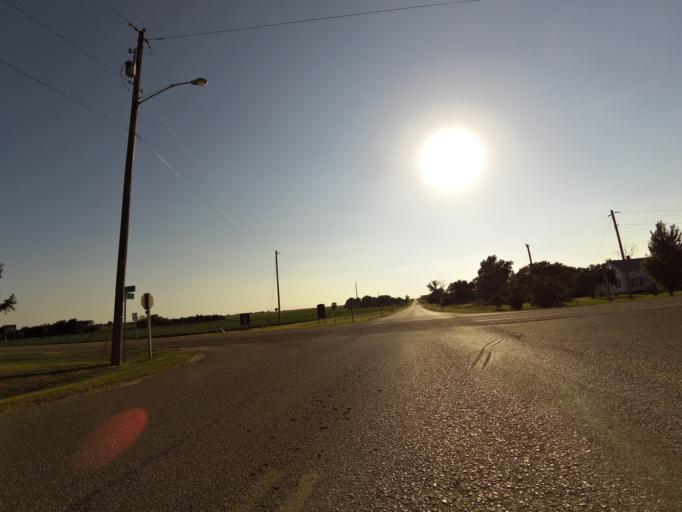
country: US
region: Kansas
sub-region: Reno County
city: Buhler
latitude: 38.1448
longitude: -97.7757
